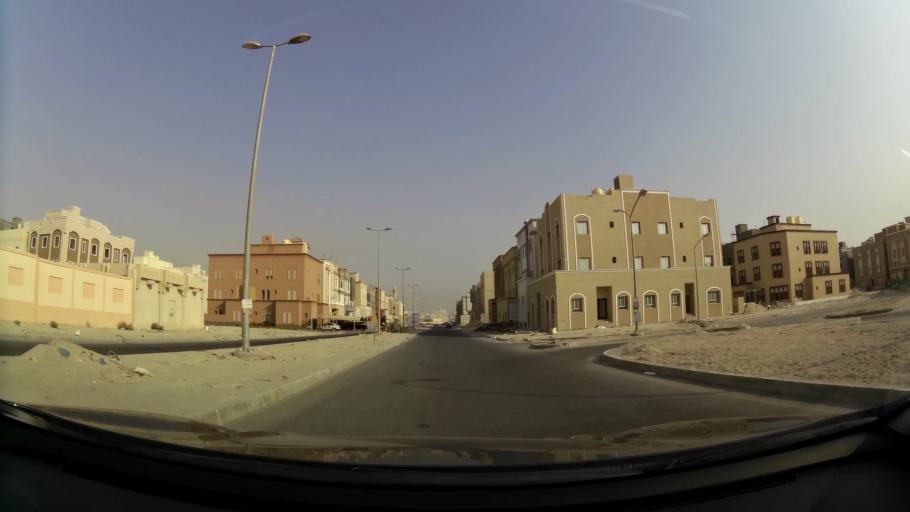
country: KW
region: Al Asimah
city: Ar Rabiyah
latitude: 29.3239
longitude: 47.8107
